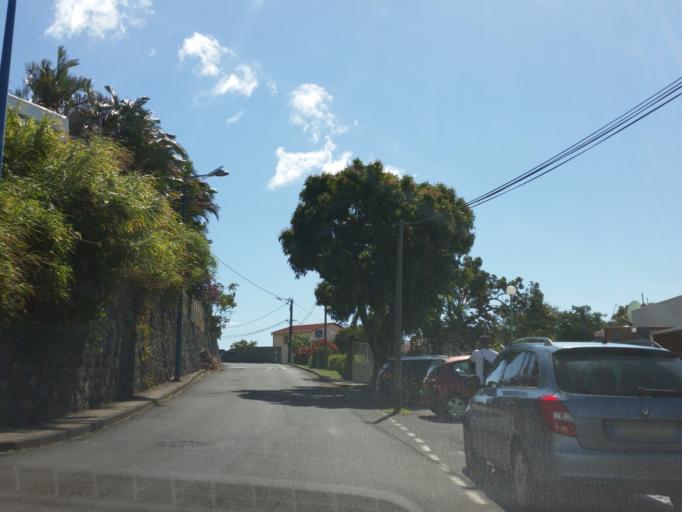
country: RE
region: Reunion
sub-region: Reunion
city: Sainte-Marie
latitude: -20.9261
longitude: 55.5257
